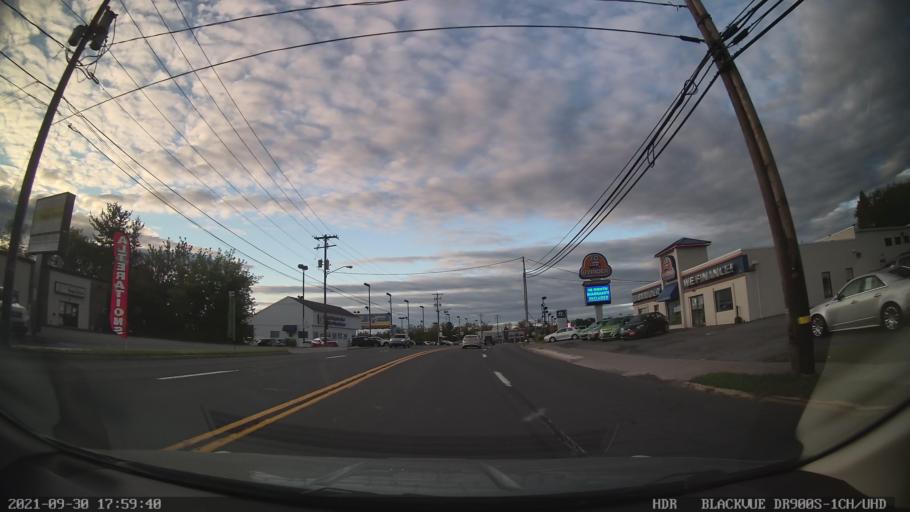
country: US
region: Pennsylvania
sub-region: Lehigh County
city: Emmaus
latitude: 40.5496
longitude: -75.4909
